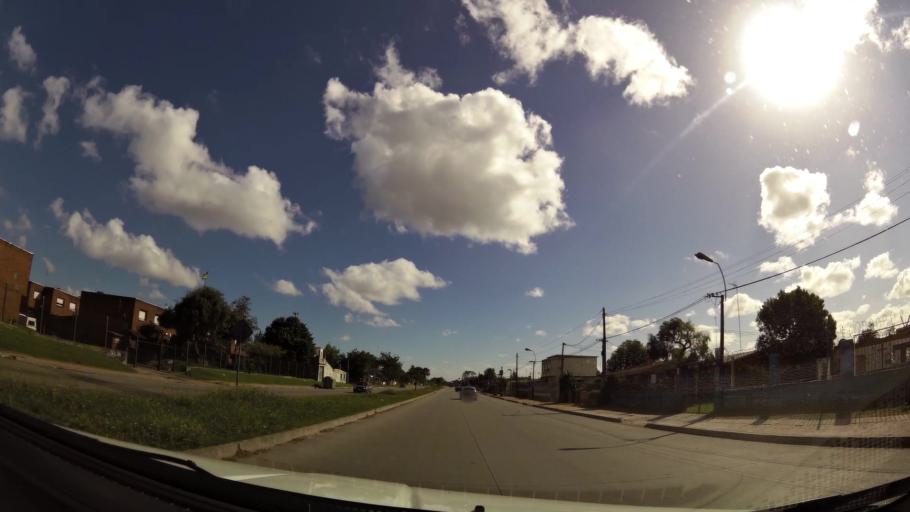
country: UY
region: Canelones
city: La Paz
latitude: -34.8113
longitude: -56.2286
